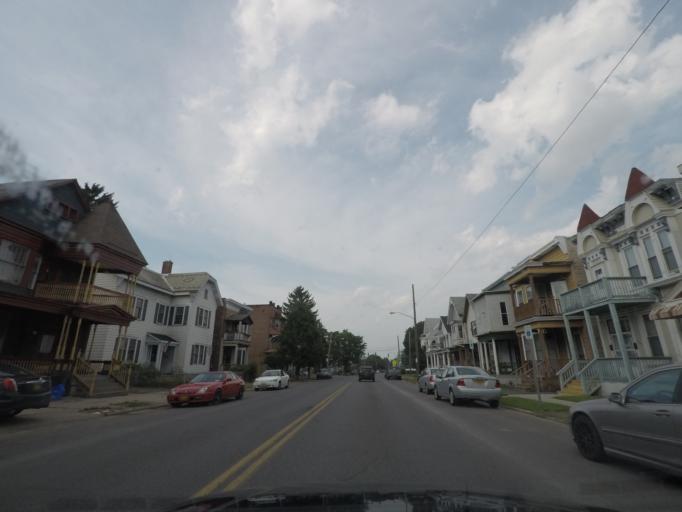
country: US
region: New York
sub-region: Albany County
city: Green Island
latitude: 42.7582
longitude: -73.6806
